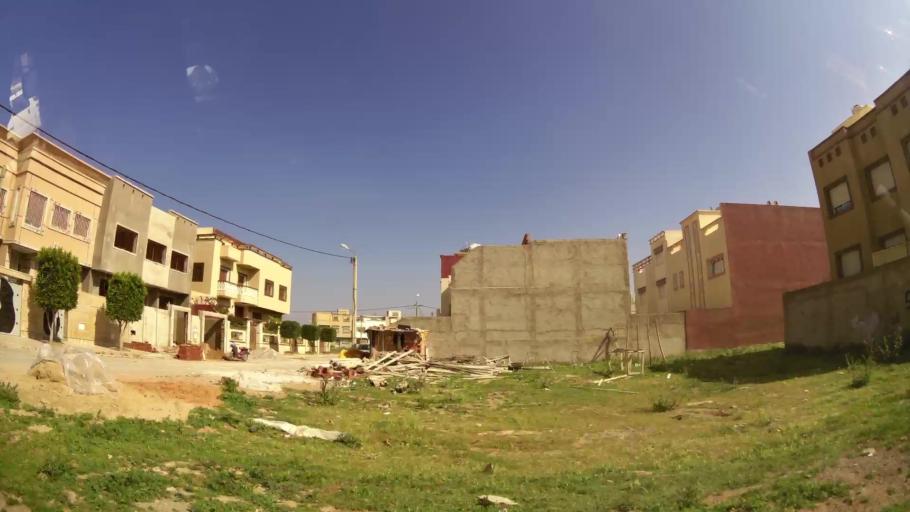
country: MA
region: Oriental
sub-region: Oujda-Angad
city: Oujda
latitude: 34.6993
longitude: -1.8820
